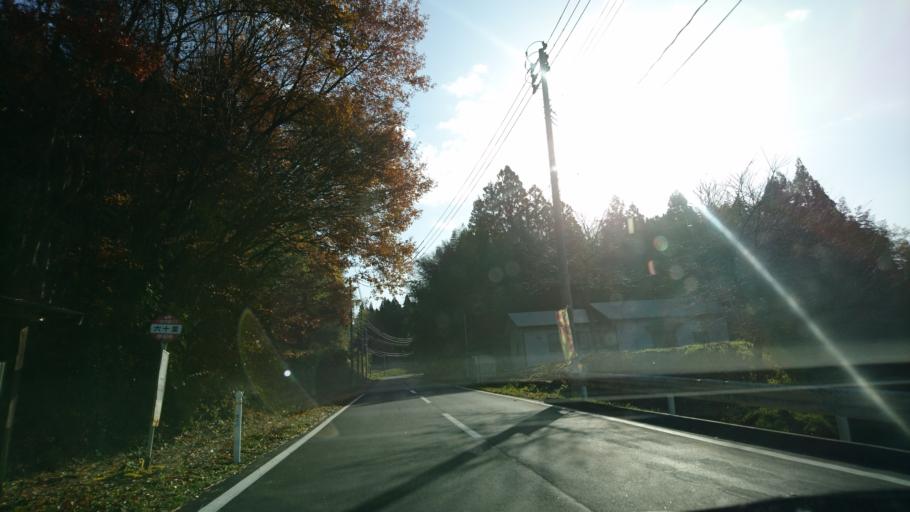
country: JP
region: Iwate
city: Ichinoseki
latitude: 38.8739
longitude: 141.3177
